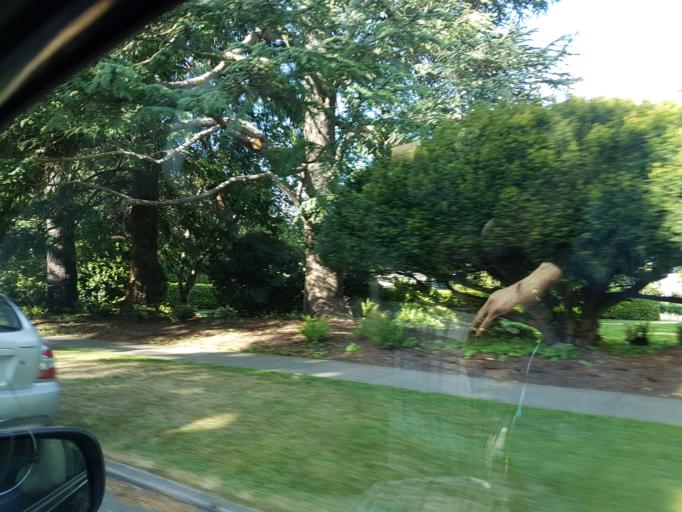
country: CA
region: British Columbia
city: Oak Bay
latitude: 48.4457
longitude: -123.2935
